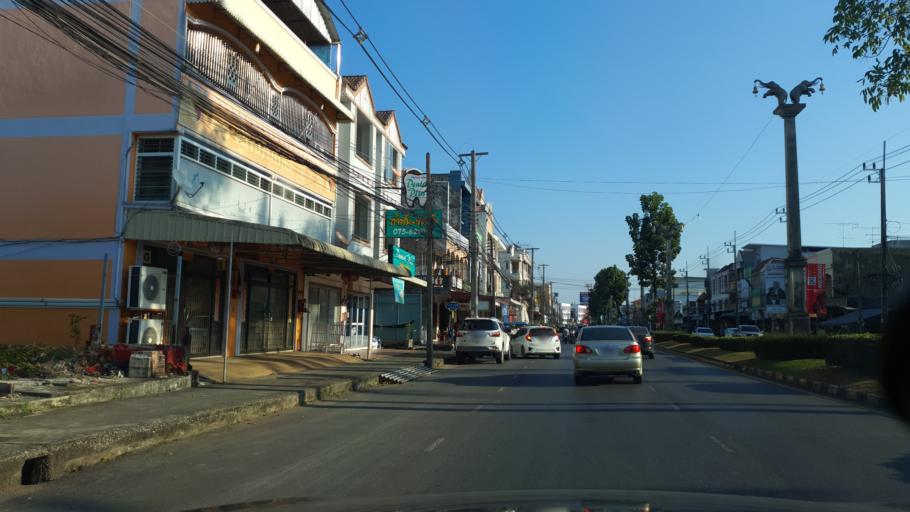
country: TH
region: Krabi
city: Krabi
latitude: 8.0700
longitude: 98.9131
